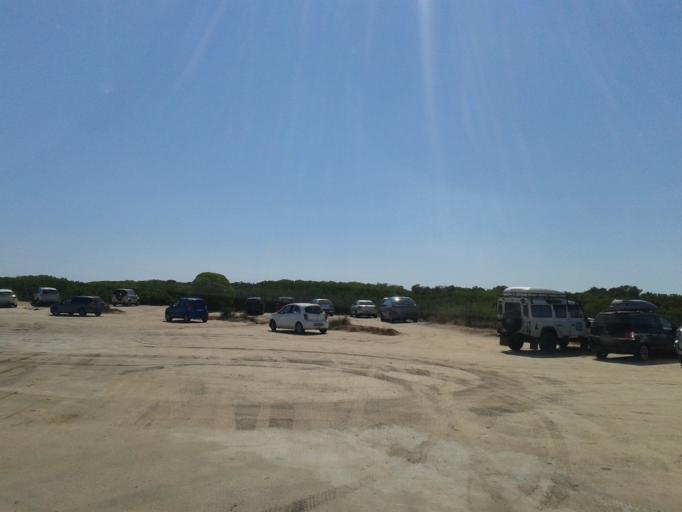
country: IT
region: Sardinia
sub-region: Provincia di Cagliari
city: Olia Speciosa
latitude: 39.2696
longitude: 9.5829
